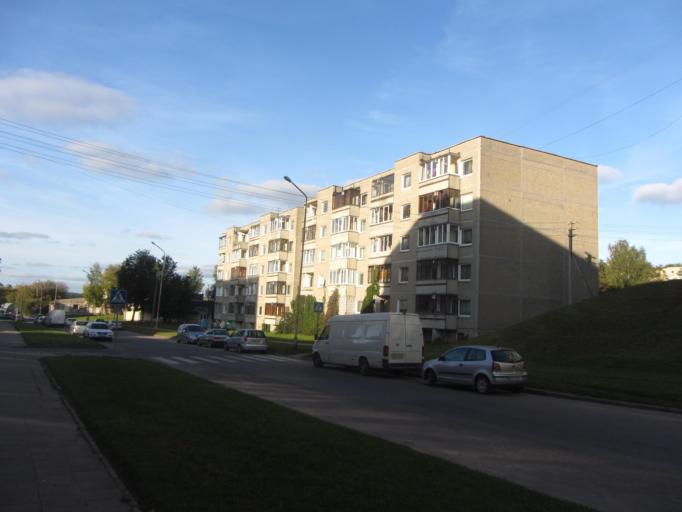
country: LT
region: Vilnius County
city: Lazdynai
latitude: 54.6407
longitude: 25.2057
